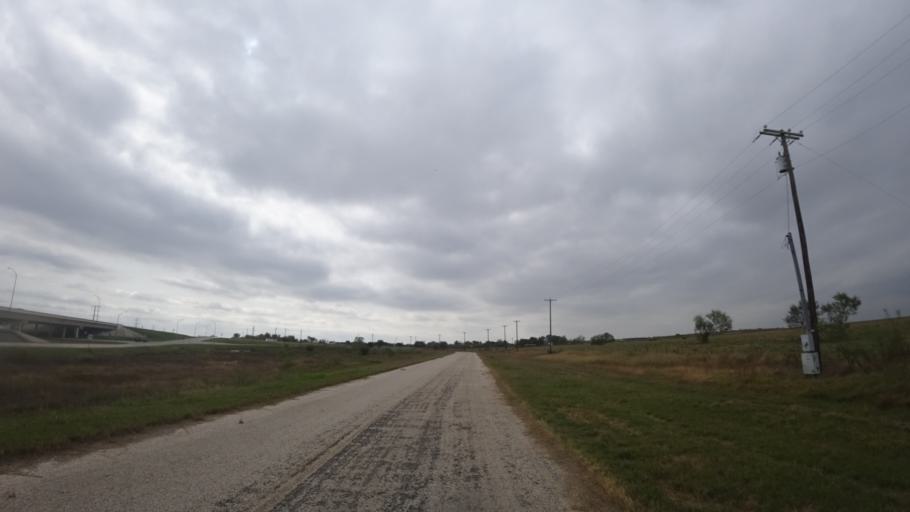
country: US
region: Texas
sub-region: Travis County
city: Pflugerville
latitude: 30.4065
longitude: -97.5847
